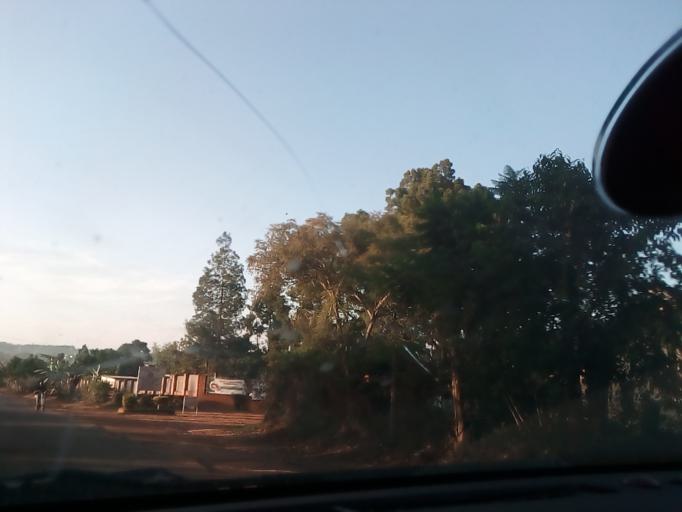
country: UG
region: Central Region
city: Masaka
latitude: -0.3290
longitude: 31.7610
